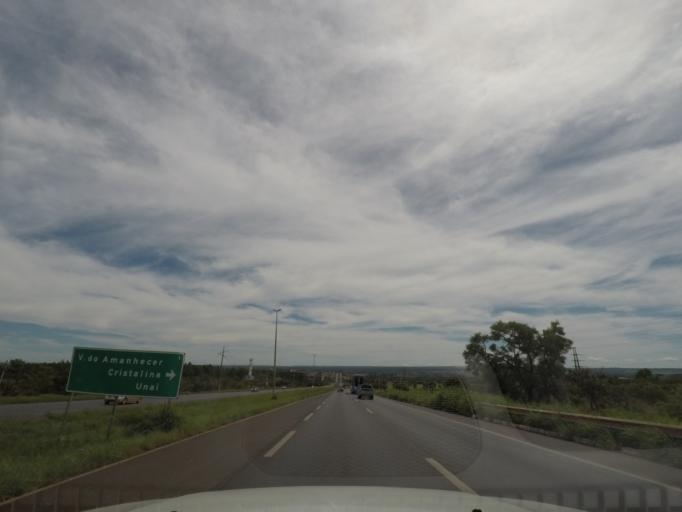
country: BR
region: Goias
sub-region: Planaltina
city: Planaltina
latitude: -15.6162
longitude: -47.7079
